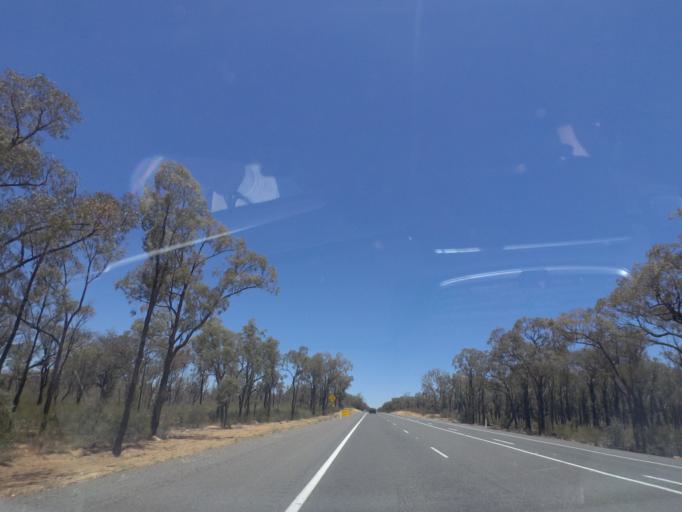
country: AU
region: New South Wales
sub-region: Warrumbungle Shire
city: Coonabarabran
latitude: -30.8999
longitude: 149.4396
